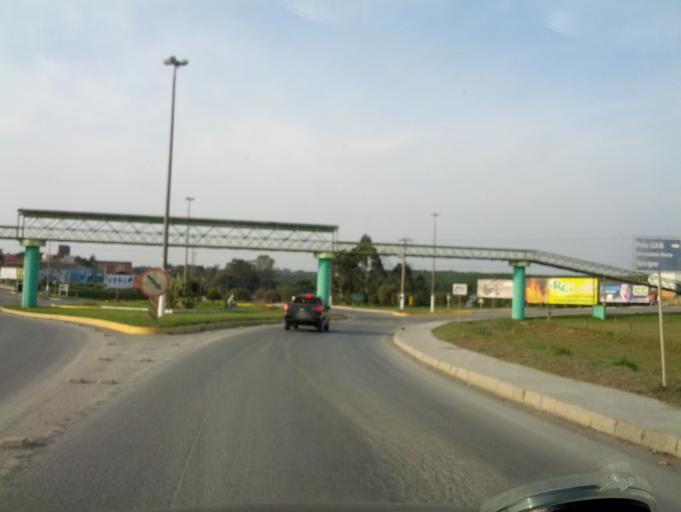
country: BR
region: Santa Catarina
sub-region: Otacilio Costa
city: Otacilio Costa
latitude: -27.5005
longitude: -50.1245
